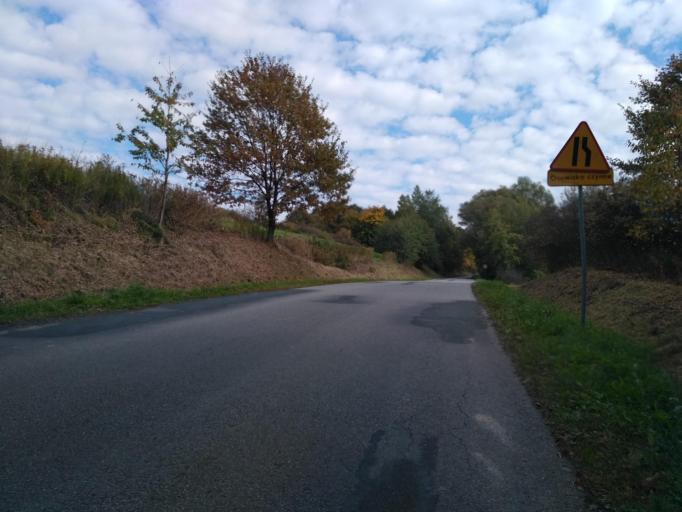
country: PL
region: Subcarpathian Voivodeship
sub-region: Powiat debicki
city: Jodlowa
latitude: 49.8929
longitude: 21.3414
